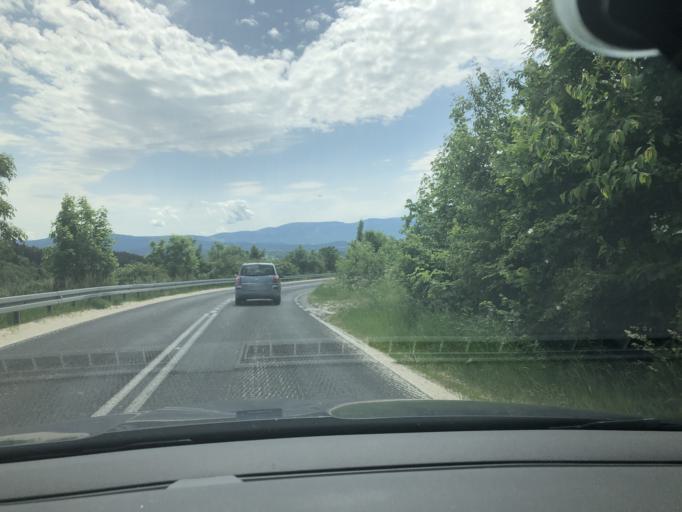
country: PL
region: Lower Silesian Voivodeship
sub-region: Powiat jeleniogorski
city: Jezow Sudecki
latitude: 50.9530
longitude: 15.8174
